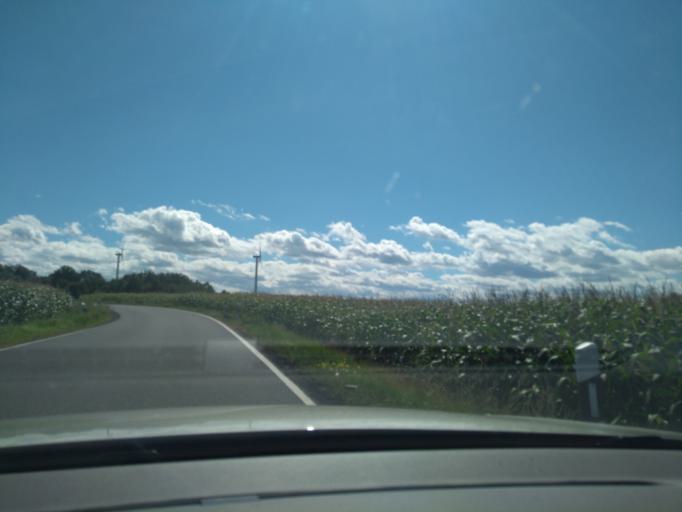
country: DE
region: Saxony
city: Lichtenberg
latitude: 51.1408
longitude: 13.9557
